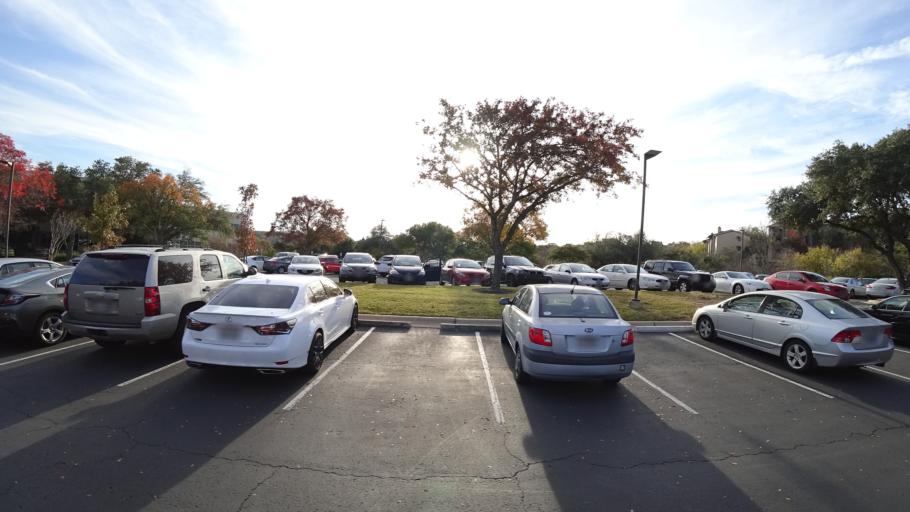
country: US
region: Texas
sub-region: Williamson County
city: Jollyville
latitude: 30.3897
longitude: -97.7564
